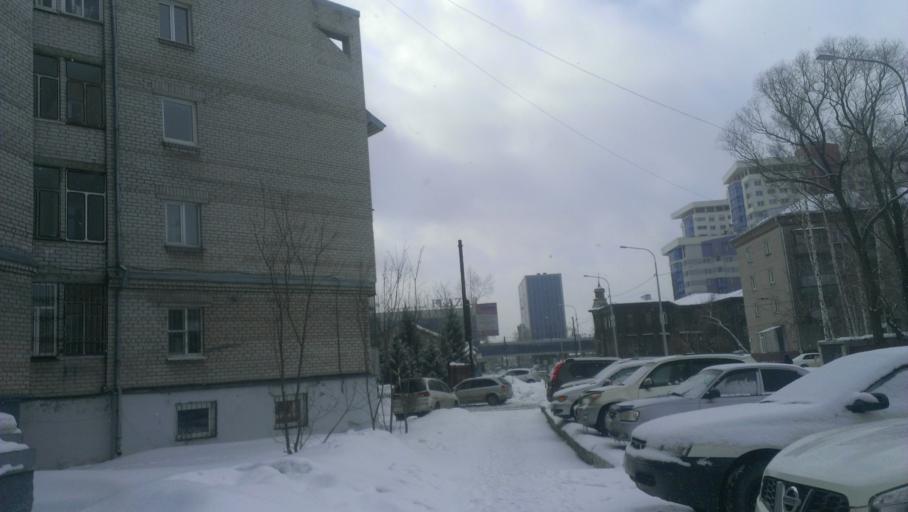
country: RU
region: Altai Krai
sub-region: Gorod Barnaulskiy
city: Barnaul
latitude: 53.3322
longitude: 83.7841
